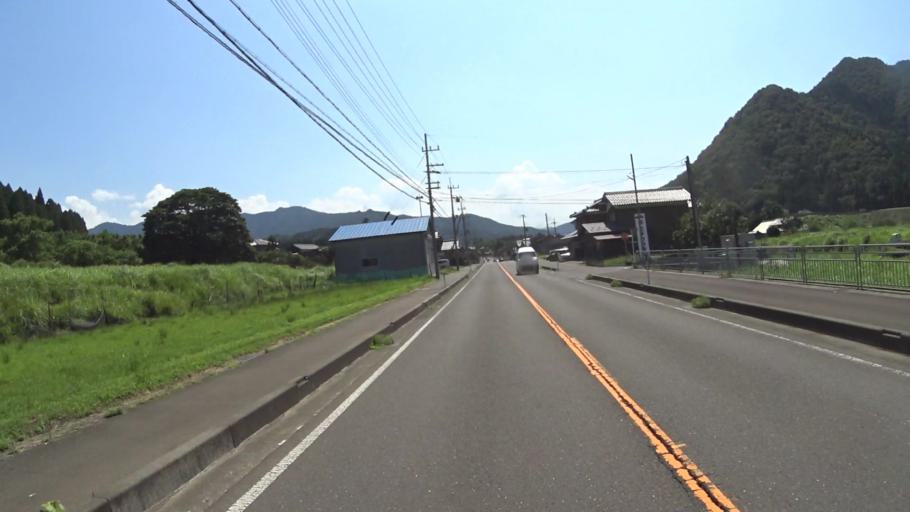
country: JP
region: Fukui
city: Obama
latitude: 35.4659
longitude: 135.7292
